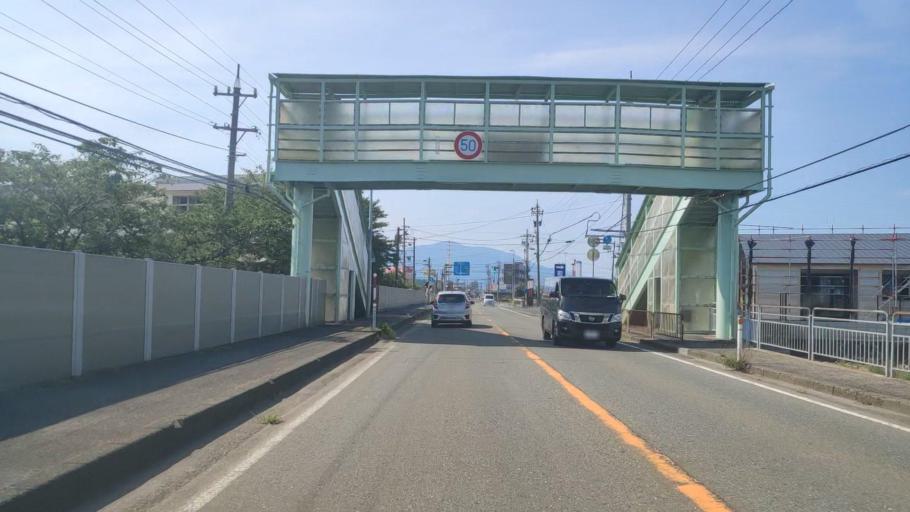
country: JP
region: Fukui
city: Tsuruga
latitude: 35.6307
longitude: 136.0720
